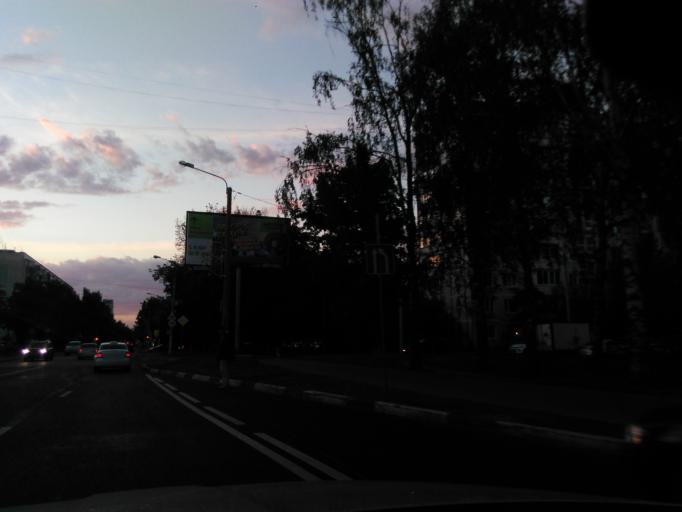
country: RU
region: Moskovskaya
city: Dolgoprudnyy
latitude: 55.9399
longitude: 37.4918
